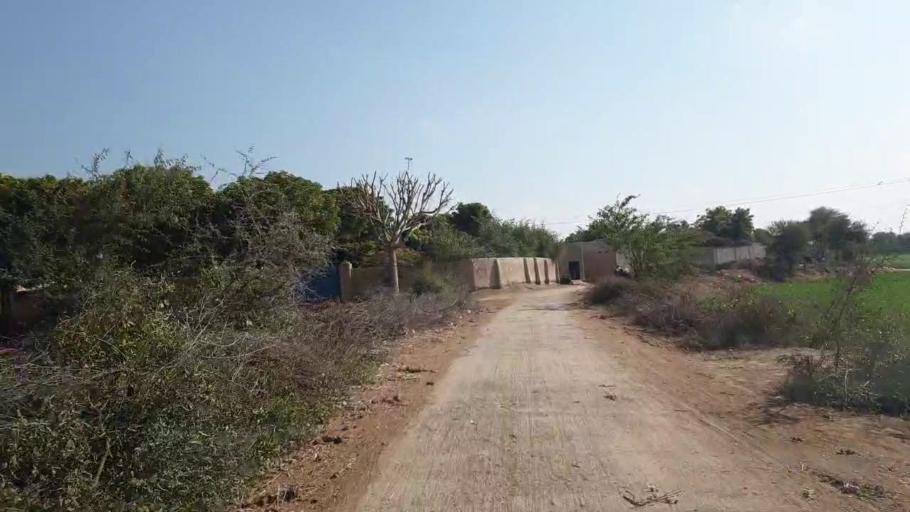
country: PK
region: Sindh
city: Shahpur Chakar
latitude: 26.0556
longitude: 68.5980
